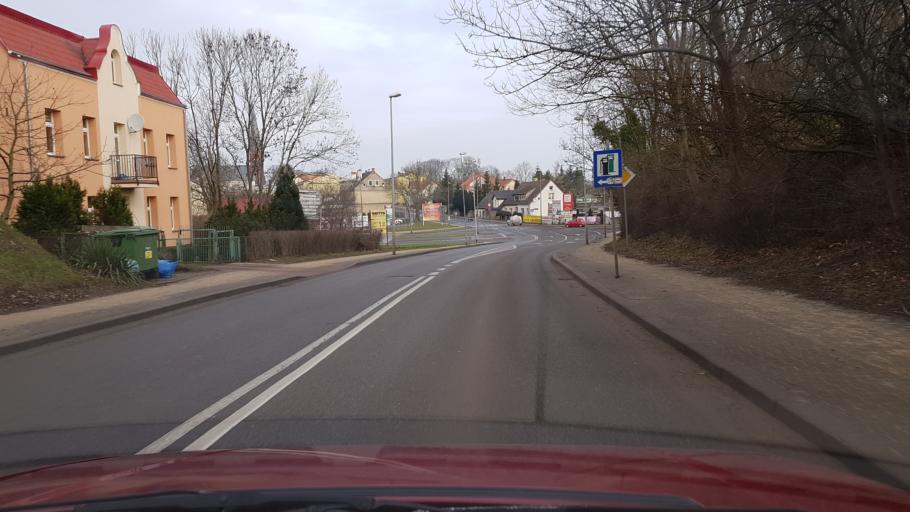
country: PL
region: West Pomeranian Voivodeship
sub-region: Powiat policki
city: Police
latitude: 53.5431
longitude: 14.5752
